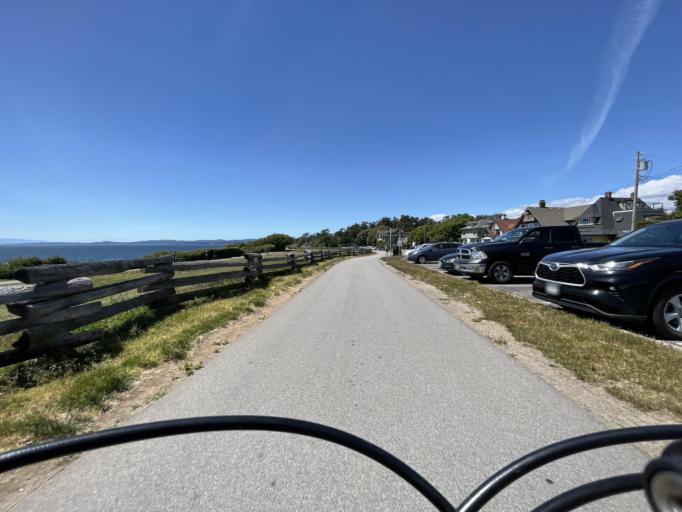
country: CA
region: British Columbia
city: Victoria
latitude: 48.4074
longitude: -123.3553
